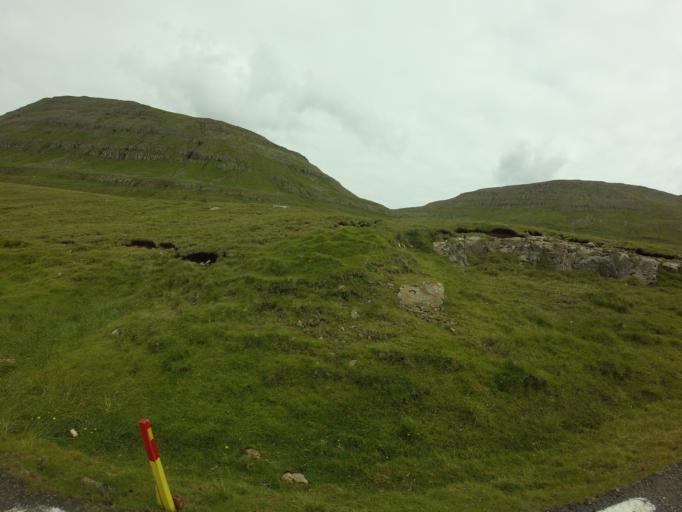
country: FO
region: Suduroy
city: Tvoroyri
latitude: 61.5189
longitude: -6.8500
